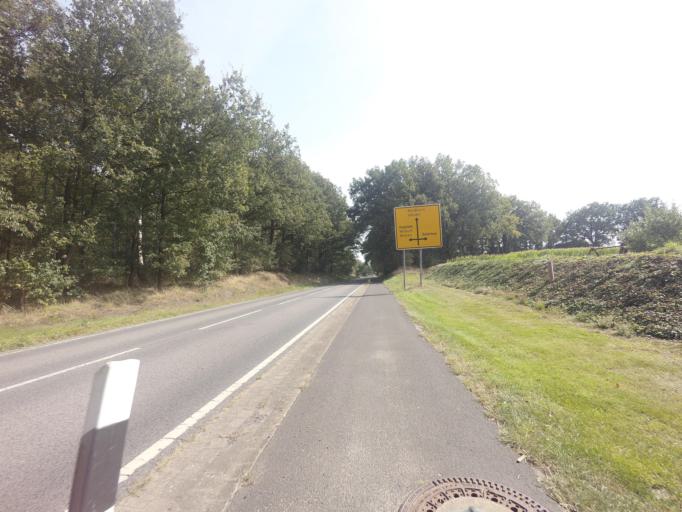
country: DE
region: Lower Saxony
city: Wielen
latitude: 52.5285
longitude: 6.7255
